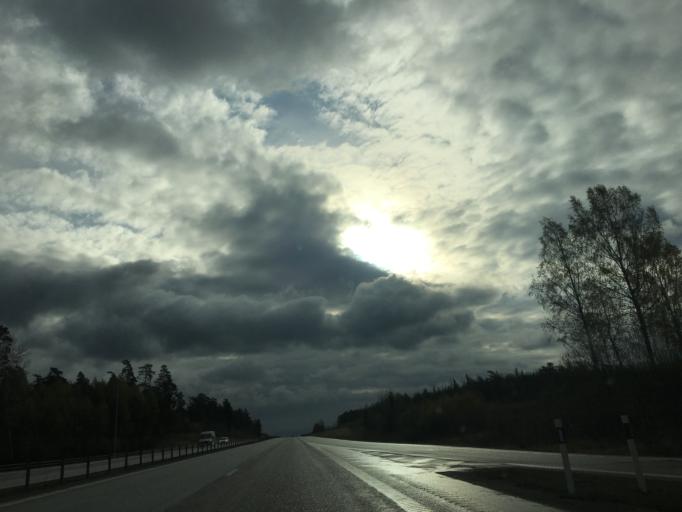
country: SE
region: Vaermland
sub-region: Karlstads Kommun
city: Skattkarr
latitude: 59.4026
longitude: 13.6181
